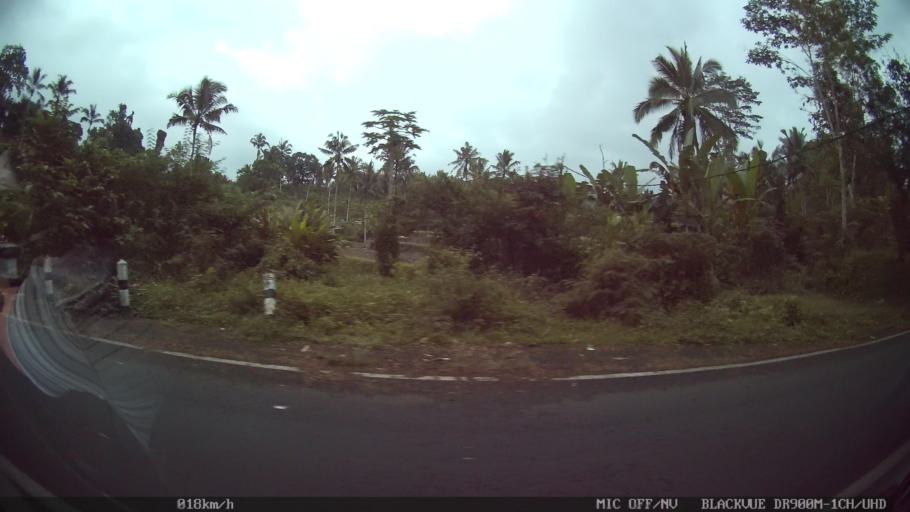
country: ID
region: Bali
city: Peneng
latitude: -8.3619
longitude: 115.1826
